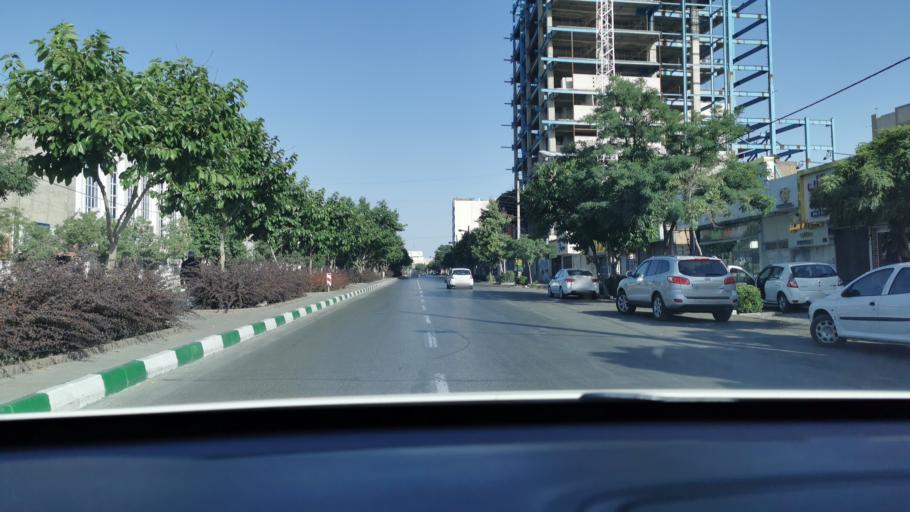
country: IR
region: Razavi Khorasan
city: Mashhad
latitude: 36.3321
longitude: 59.5169
